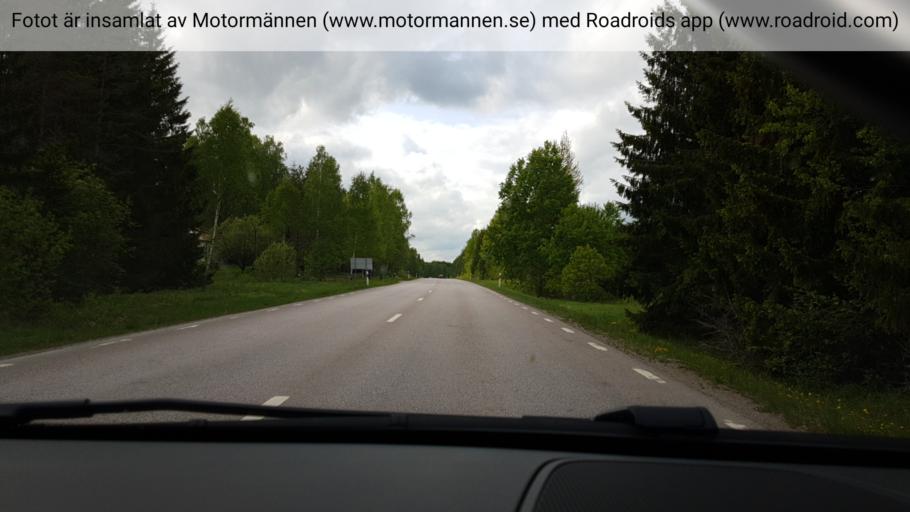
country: SE
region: Uppsala
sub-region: Tierps Kommun
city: Orbyhus
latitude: 60.2583
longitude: 17.6291
